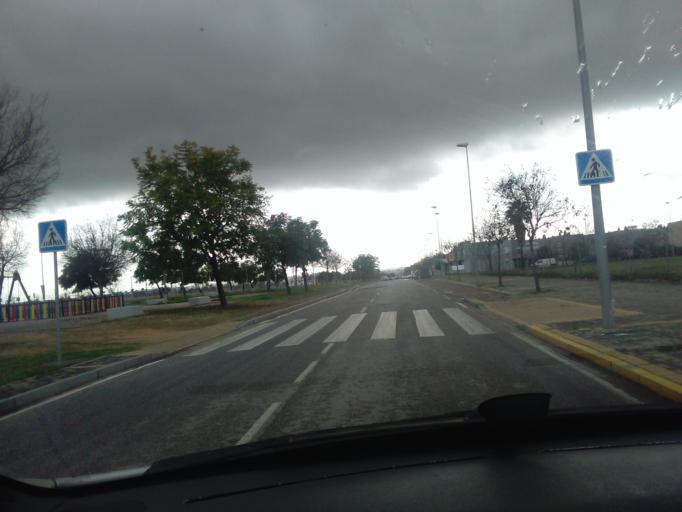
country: ES
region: Andalusia
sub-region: Provincia de Sevilla
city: Sevilla
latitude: 37.3815
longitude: -5.9147
